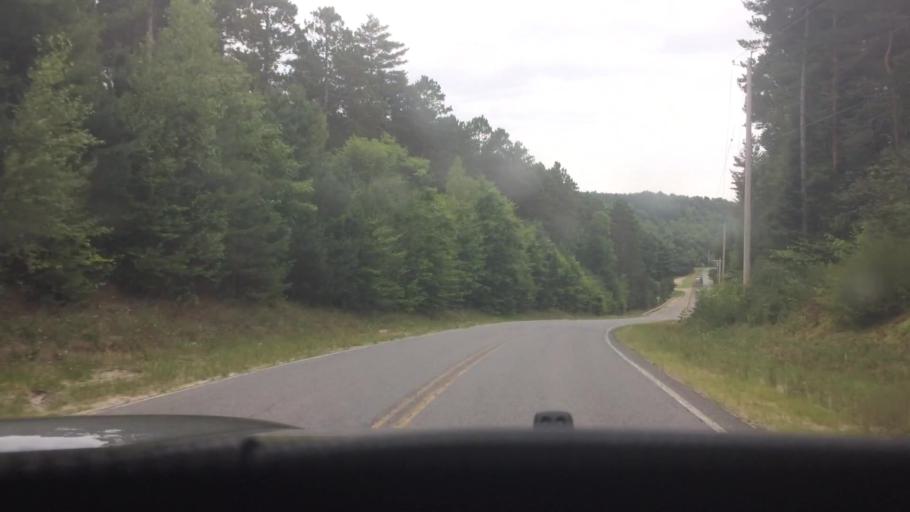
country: US
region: New York
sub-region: St. Lawrence County
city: Hannawa Falls
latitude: 44.5614
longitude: -74.9243
